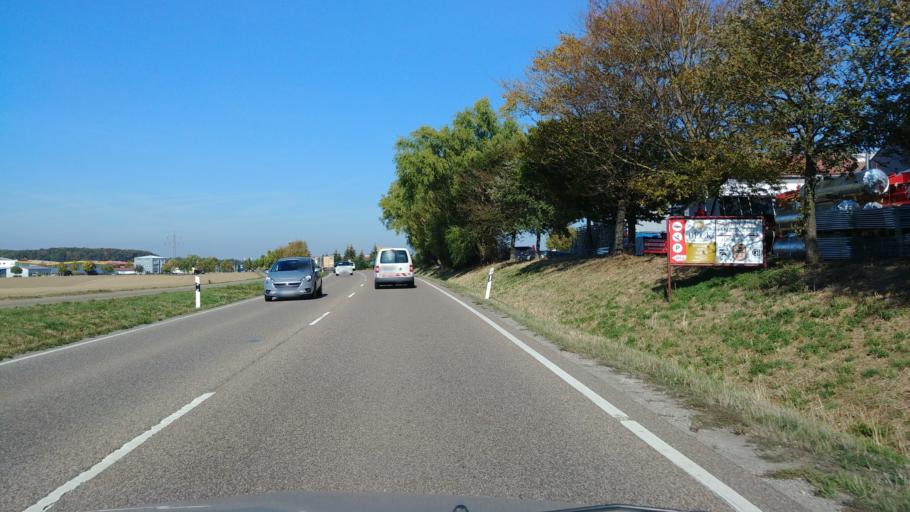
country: DE
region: Baden-Wuerttemberg
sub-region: Regierungsbezirk Stuttgart
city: Untermunkheim
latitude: 49.1741
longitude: 9.7123
